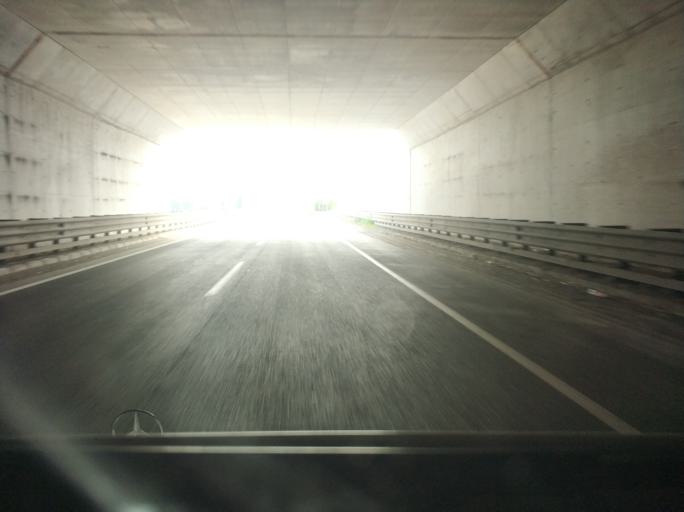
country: TR
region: Sivas
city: Yildizeli
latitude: 39.8549
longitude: 36.5425
